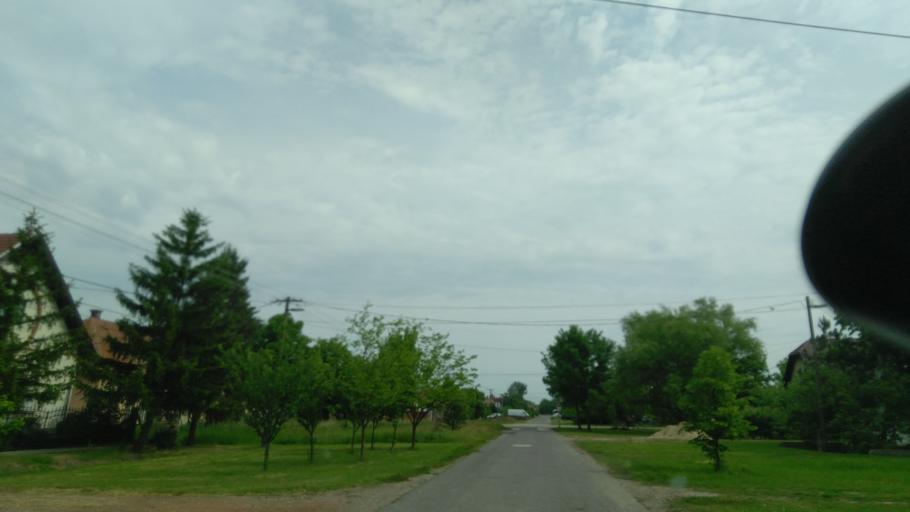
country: HU
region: Bekes
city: Szeghalom
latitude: 47.0202
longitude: 21.1680
